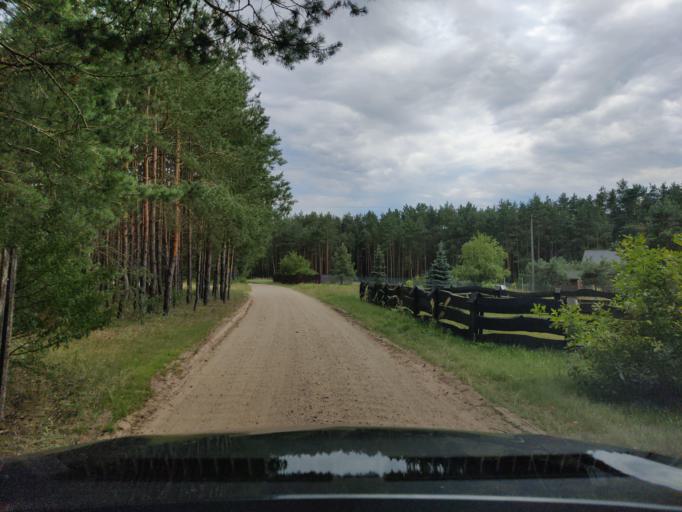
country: PL
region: Masovian Voivodeship
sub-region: Powiat pultuski
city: Pultusk
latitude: 52.7624
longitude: 21.1332
